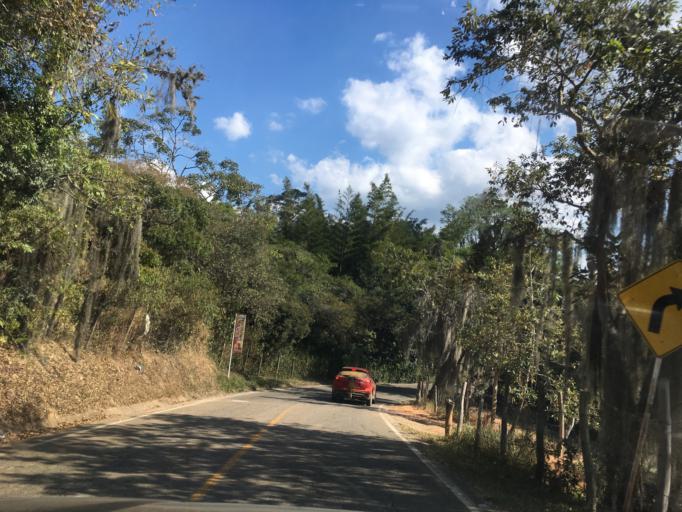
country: CO
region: Santander
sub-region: San Gil
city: San Gil
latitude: 6.5925
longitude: -73.1586
